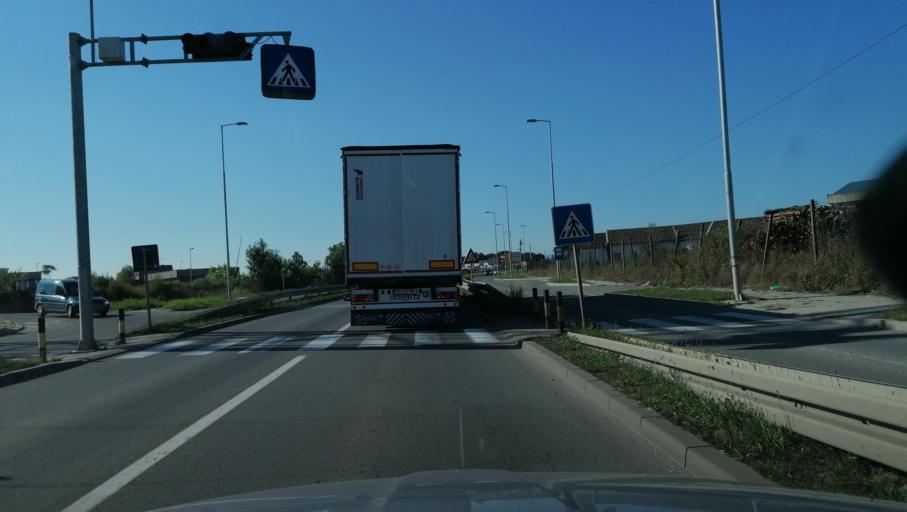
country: RS
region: Central Serbia
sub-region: Raski Okrug
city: Kraljevo
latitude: 43.7405
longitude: 20.6656
